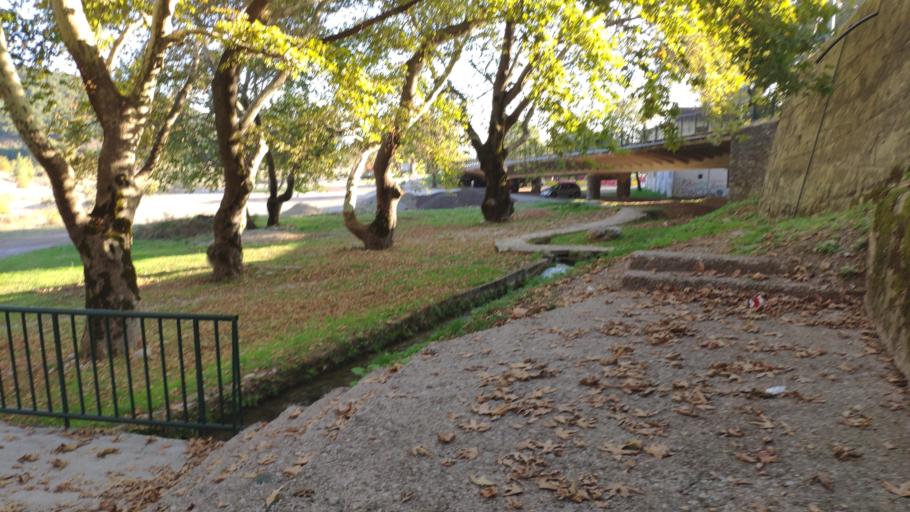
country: GR
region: Thessaly
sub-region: Trikala
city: Pyli
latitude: 39.4589
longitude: 21.6130
